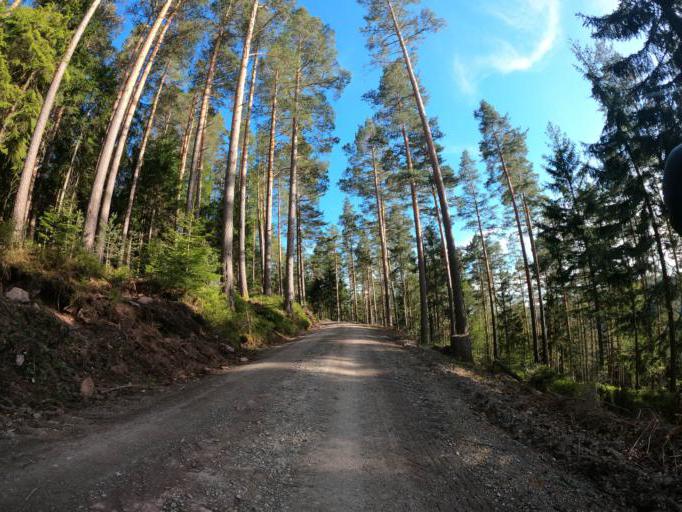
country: DE
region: Baden-Wuerttemberg
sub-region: Karlsruhe Region
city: Bad Wildbad
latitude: 48.7092
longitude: 8.5681
